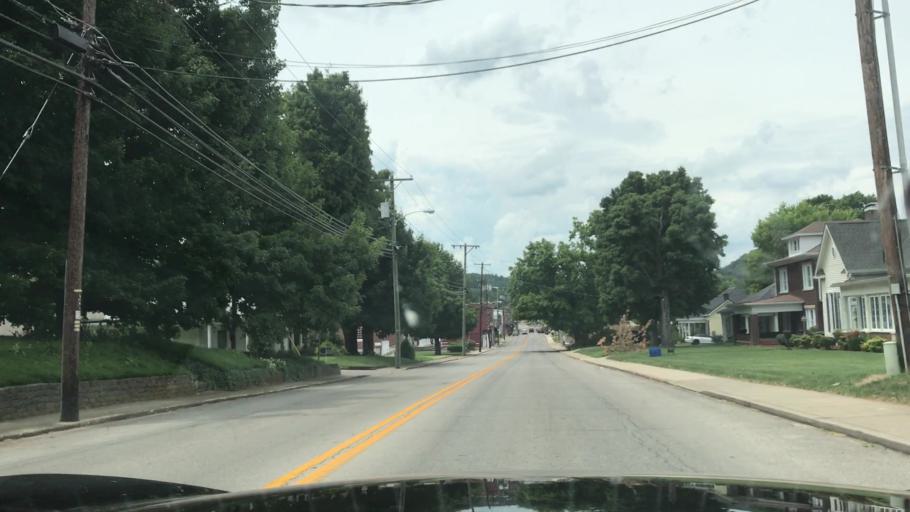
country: US
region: Kentucky
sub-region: Hart County
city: Horse Cave
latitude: 37.1790
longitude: -85.9021
